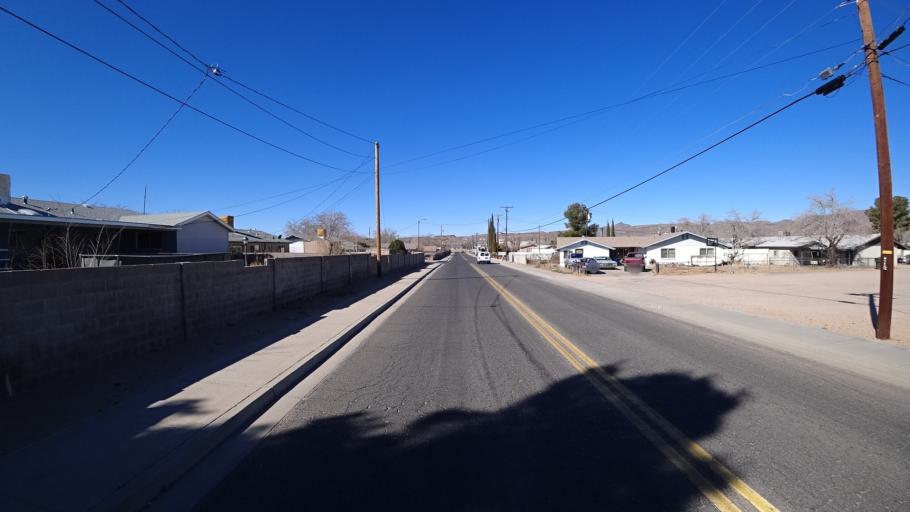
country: US
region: Arizona
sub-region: Mohave County
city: Kingman
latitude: 35.2140
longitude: -114.0207
